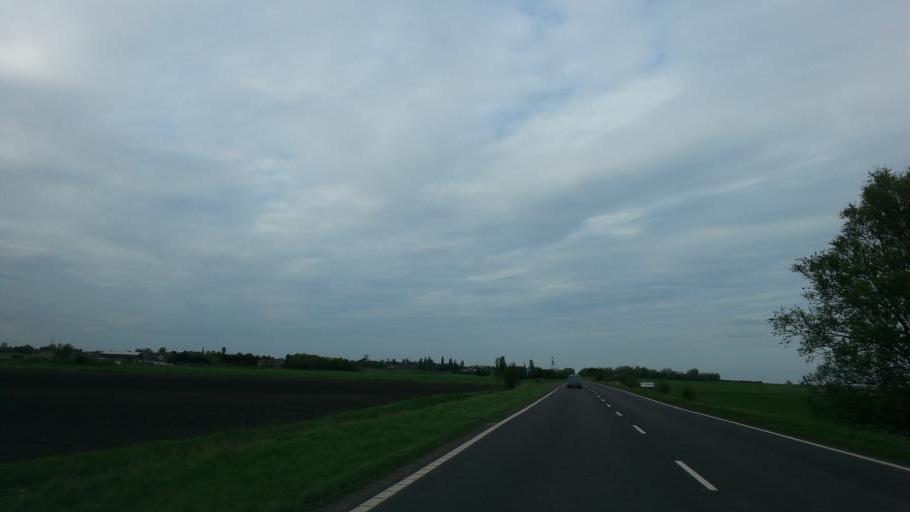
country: GB
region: England
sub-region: Cambridgeshire
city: Doddington
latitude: 52.4808
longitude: 0.0589
